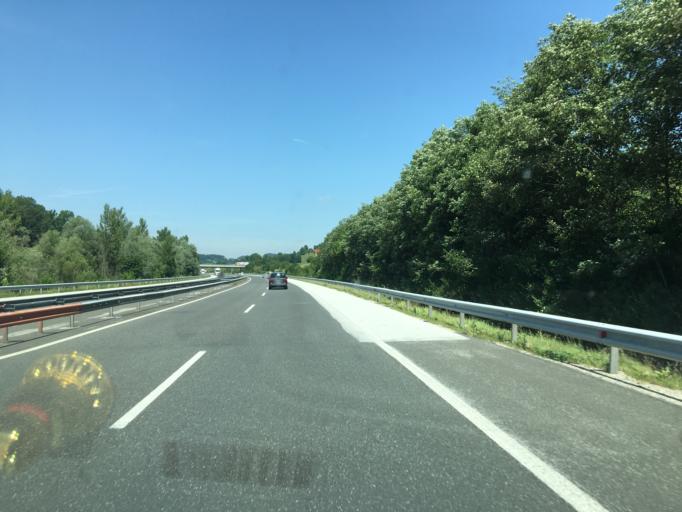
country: SI
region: Pesnica
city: Pesnica pri Mariboru
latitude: 46.6337
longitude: 15.6573
